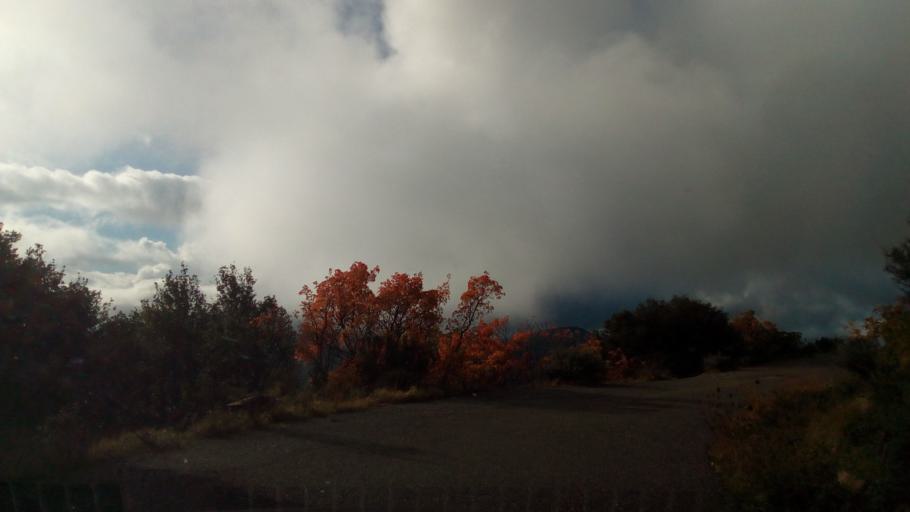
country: GR
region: West Greece
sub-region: Nomos Aitolias kai Akarnanias
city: Nafpaktos
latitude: 38.5185
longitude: 21.9488
